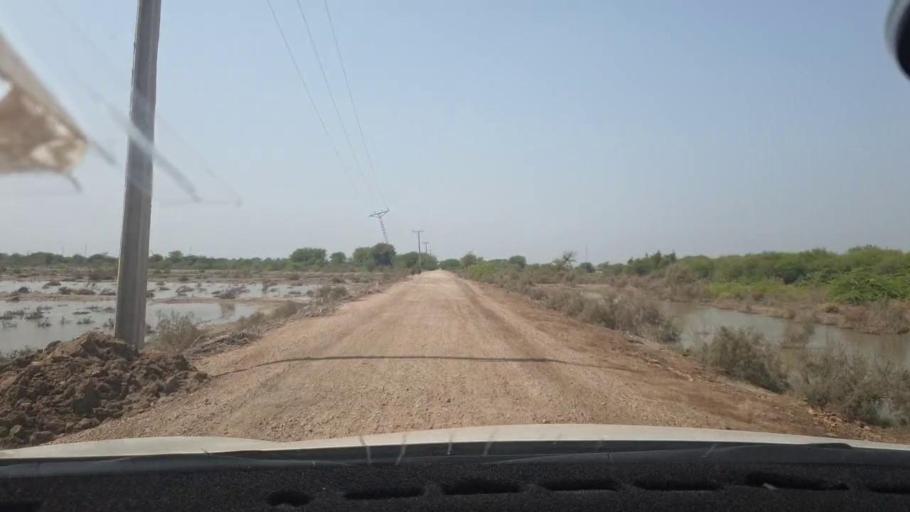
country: PK
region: Sindh
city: Tando Mittha Khan
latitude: 25.9204
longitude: 69.2523
